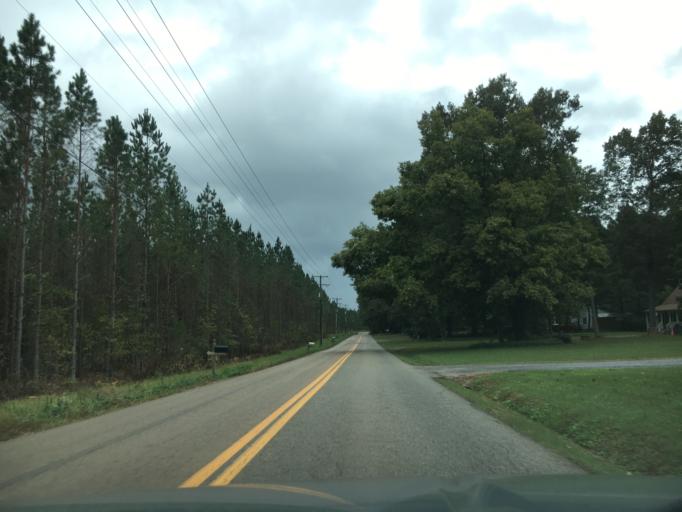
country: US
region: Virginia
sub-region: Amelia County
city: Amelia Court House
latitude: 37.3659
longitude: -77.9766
